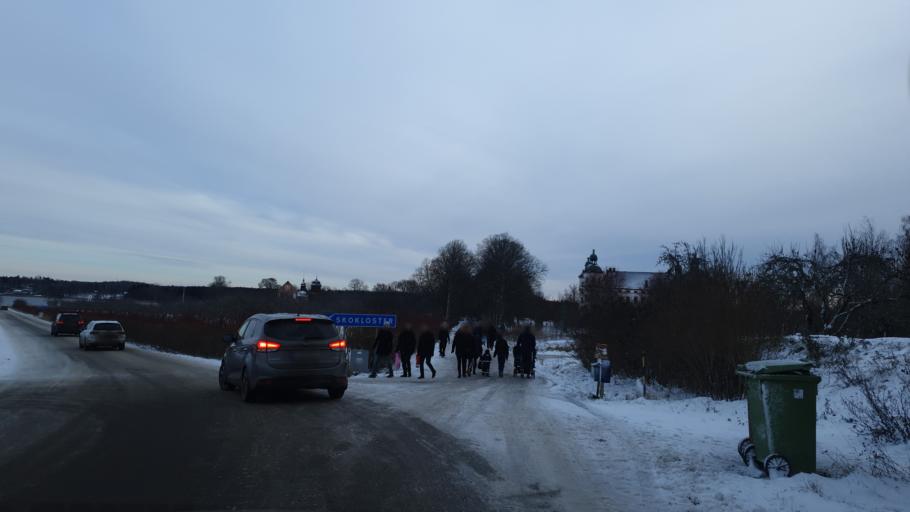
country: SE
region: Stockholm
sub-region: Sigtuna Kommun
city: Sigtuna
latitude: 59.7051
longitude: 17.6156
